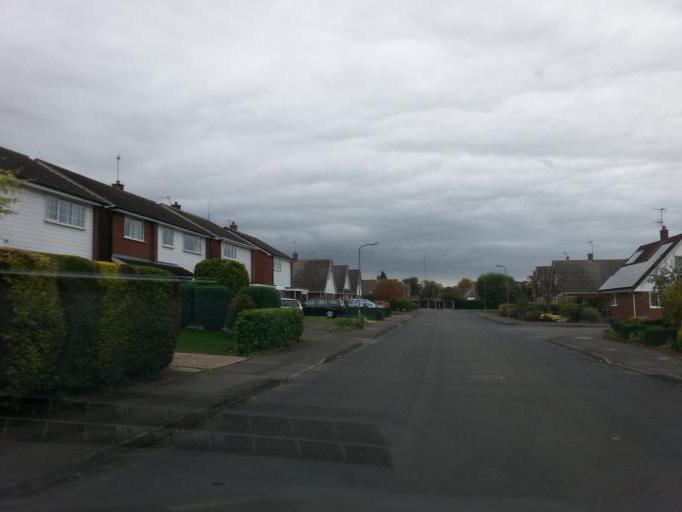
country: GB
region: England
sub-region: Nottinghamshire
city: Newark on Trent
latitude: 53.0755
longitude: -0.7805
